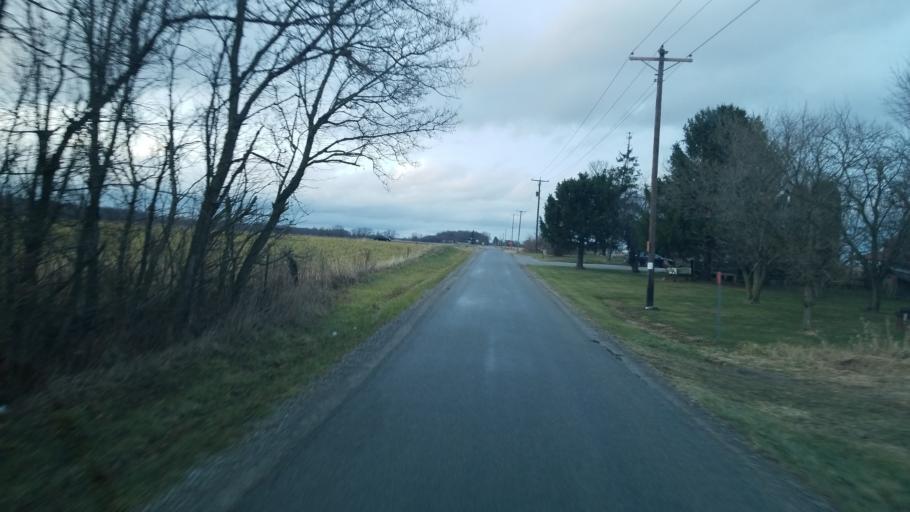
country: US
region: Ohio
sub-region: Delaware County
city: Ashley
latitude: 40.4555
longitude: -83.0484
